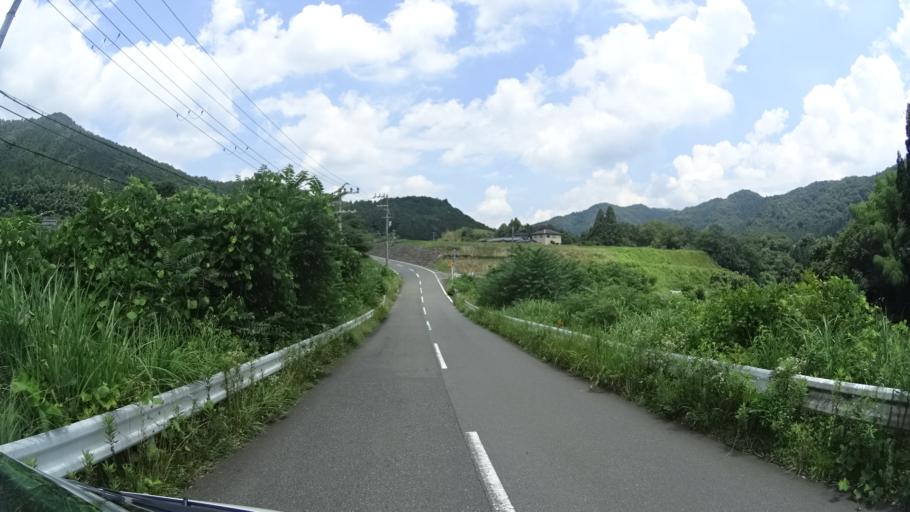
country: JP
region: Kyoto
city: Ayabe
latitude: 35.2022
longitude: 135.2438
